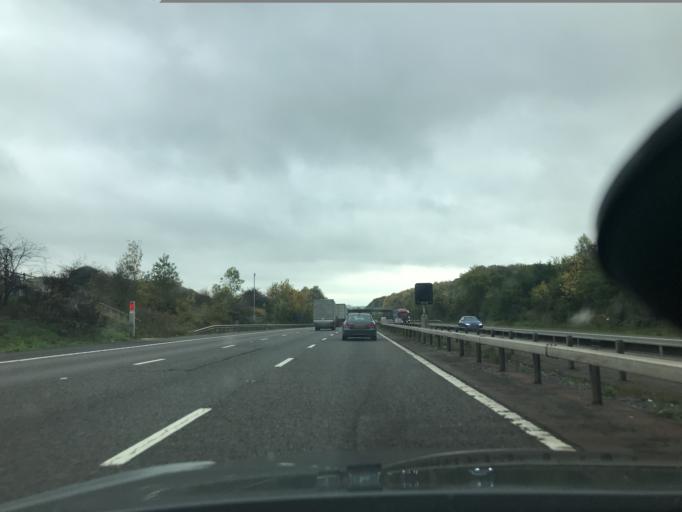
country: GB
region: England
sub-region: Warwickshire
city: Wroxall
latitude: 52.2824
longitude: -1.6617
